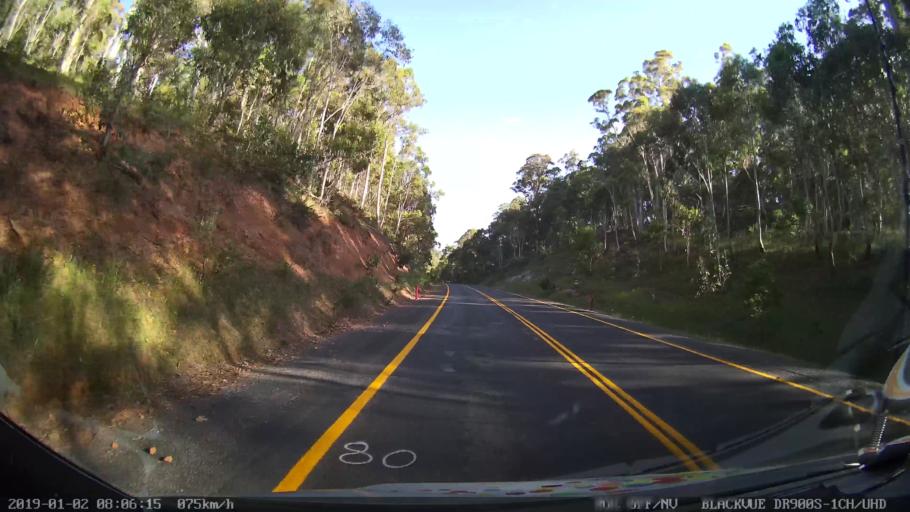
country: AU
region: New South Wales
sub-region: Tumut Shire
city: Tumut
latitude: -35.6421
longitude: 148.3872
